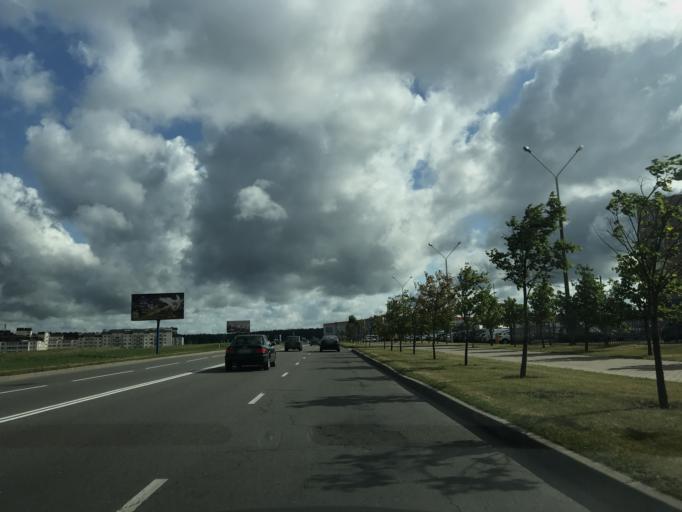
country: BY
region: Minsk
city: Borovlyany
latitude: 53.9648
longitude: 27.6210
